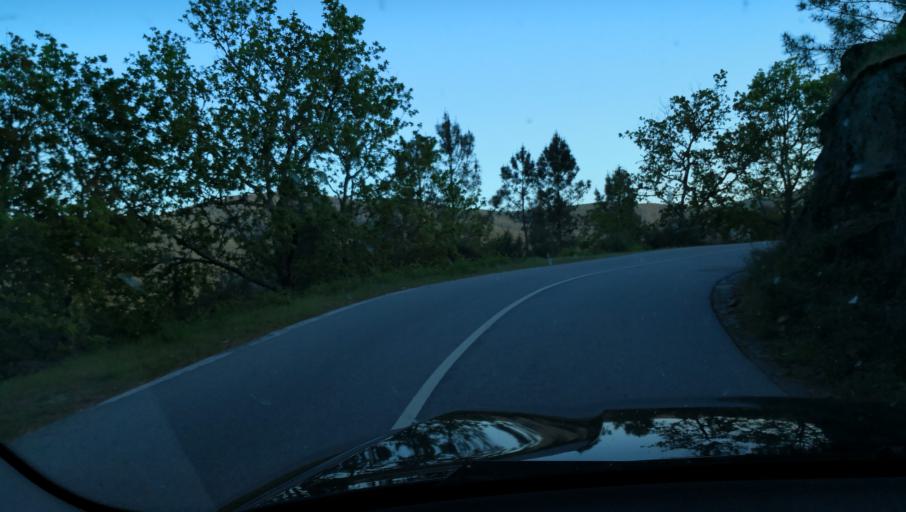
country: PT
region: Vila Real
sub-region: Mondim de Basto
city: Mondim de Basto
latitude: 41.4060
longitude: -7.9150
